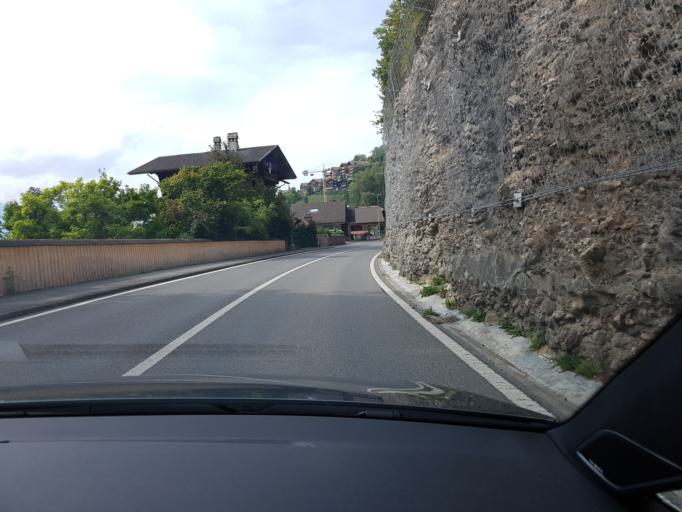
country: CH
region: Bern
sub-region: Thun District
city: Sigriswil
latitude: 46.7121
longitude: 7.7059
